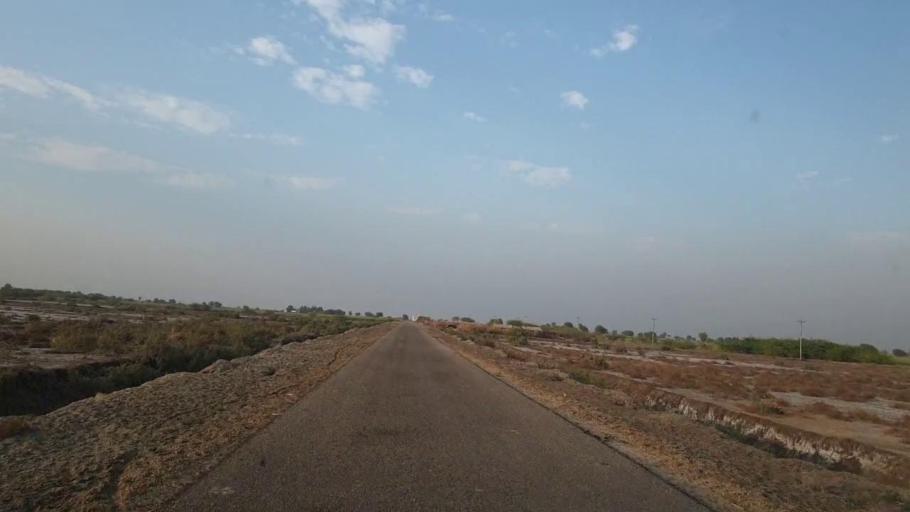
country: PK
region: Sindh
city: Pithoro
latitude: 25.5911
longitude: 69.3115
